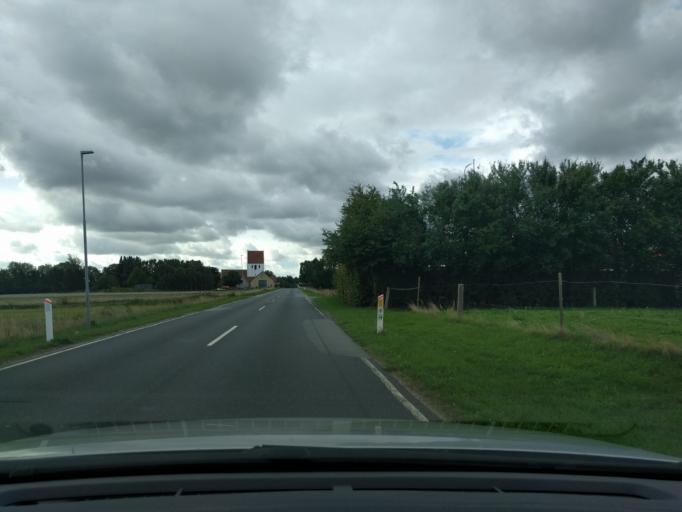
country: DK
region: South Denmark
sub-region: Nyborg Kommune
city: Ullerslev
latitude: 55.3871
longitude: 10.6668
